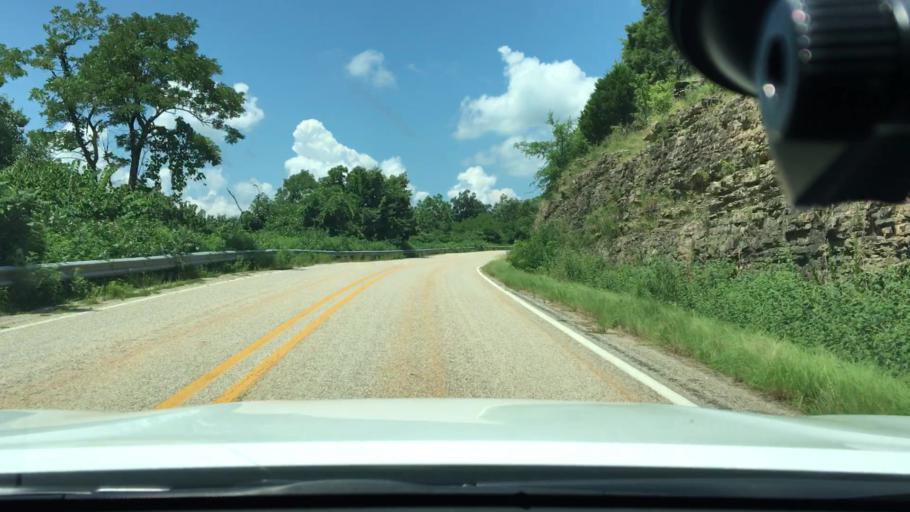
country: US
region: Arkansas
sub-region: Logan County
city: Paris
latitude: 35.1761
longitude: -93.5888
